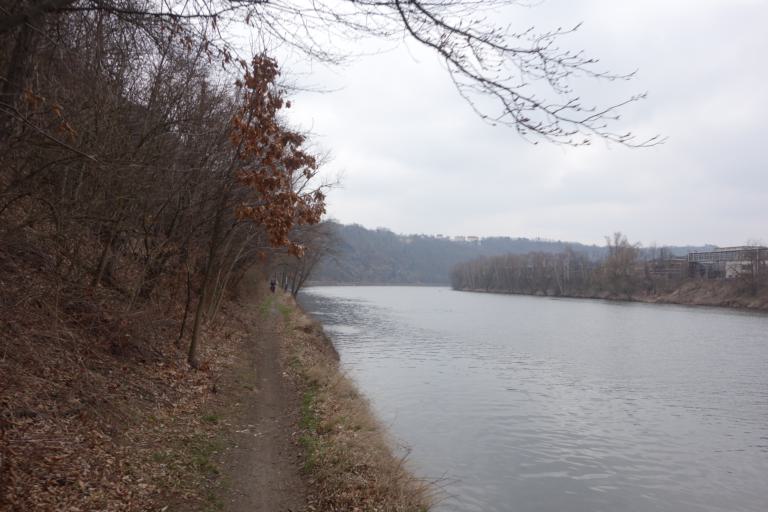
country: CZ
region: Central Bohemia
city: Libcice nad Vltavou
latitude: 50.1997
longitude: 14.3705
